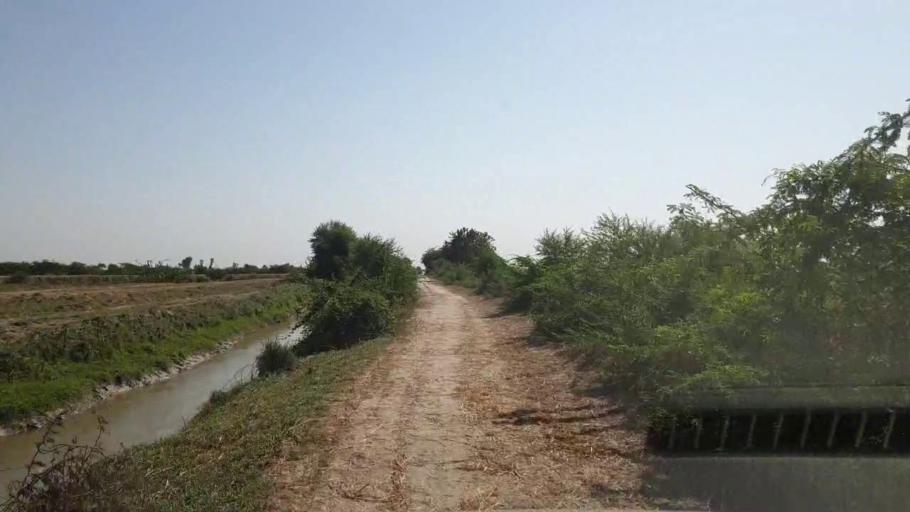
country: PK
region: Sindh
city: Kadhan
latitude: 24.6177
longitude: 68.9970
